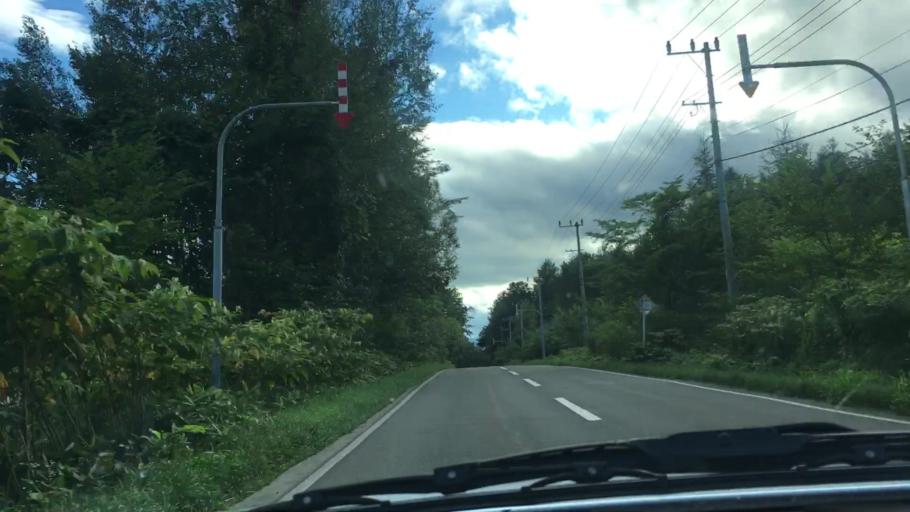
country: JP
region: Hokkaido
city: Otofuke
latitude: 43.1708
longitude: 142.9133
